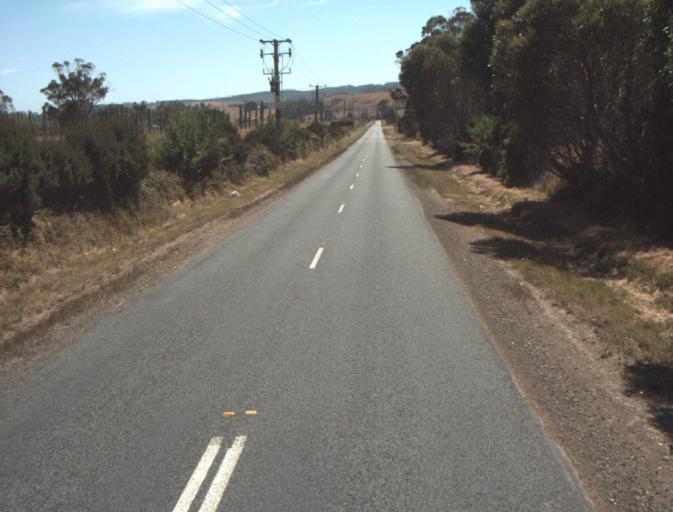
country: AU
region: Tasmania
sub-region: Launceston
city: Mayfield
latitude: -41.2565
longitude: 147.1463
